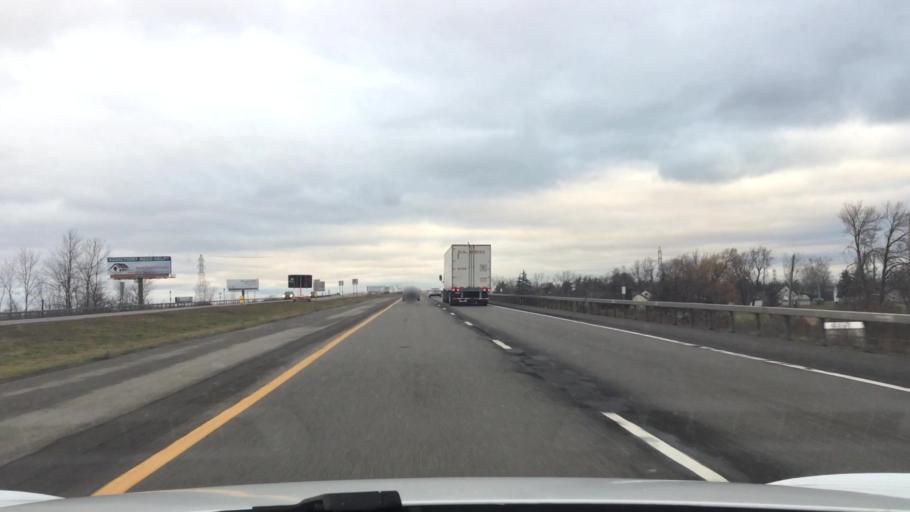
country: US
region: New York
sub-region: Niagara County
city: Niagara Falls
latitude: 43.1137
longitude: -78.9976
